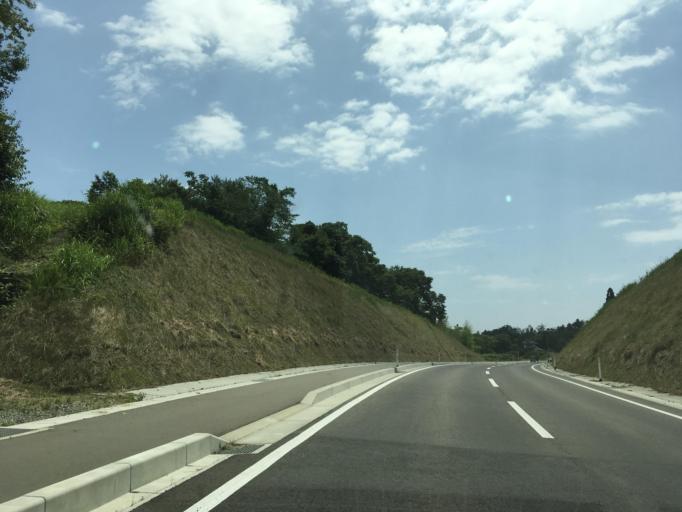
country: JP
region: Iwate
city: Ofunato
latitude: 39.0212
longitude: 141.7106
